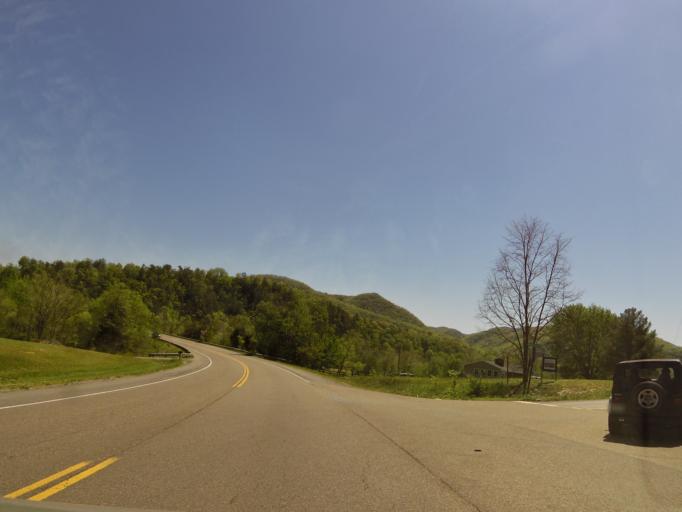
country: US
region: Tennessee
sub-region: Unicoi County
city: Erwin
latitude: 36.1809
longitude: -82.4582
